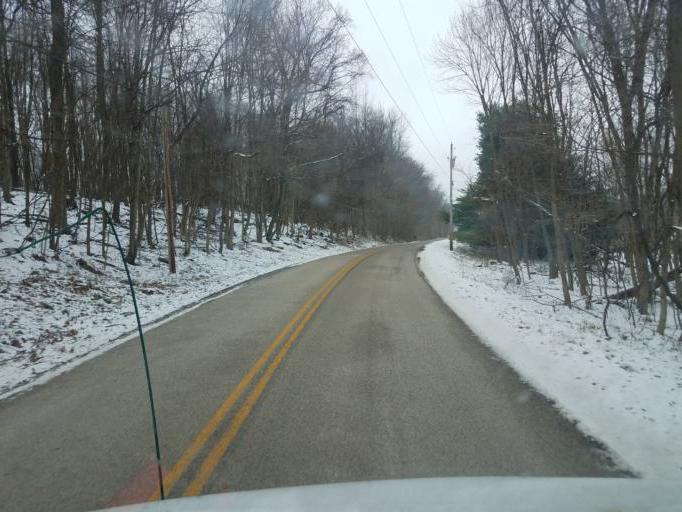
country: US
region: Ohio
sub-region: Sandusky County
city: Bellville
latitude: 40.6673
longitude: -82.4162
